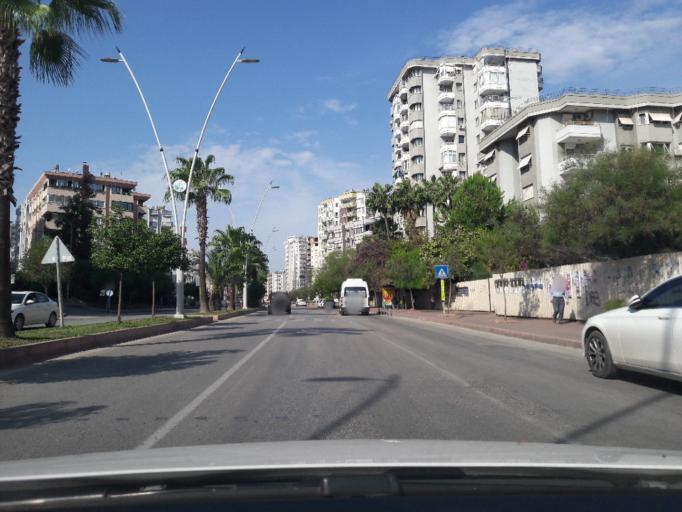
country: TR
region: Adana
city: Adana
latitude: 37.0149
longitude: 35.3257
